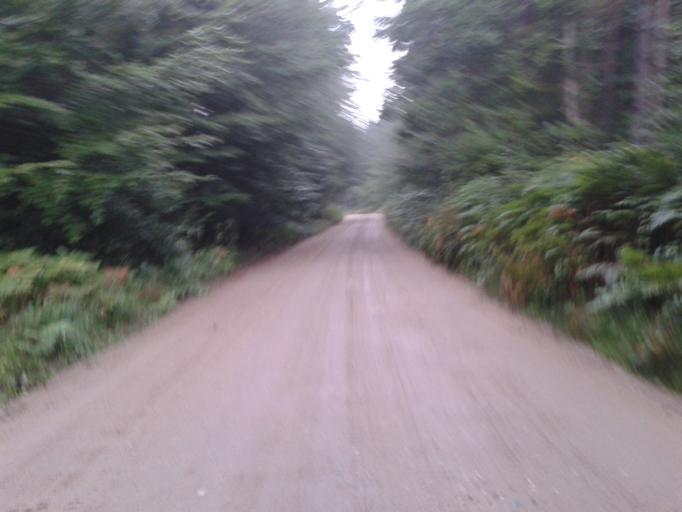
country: PL
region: Pomeranian Voivodeship
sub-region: Powiat pucki
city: Krokowa
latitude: 54.7210
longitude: 18.2311
